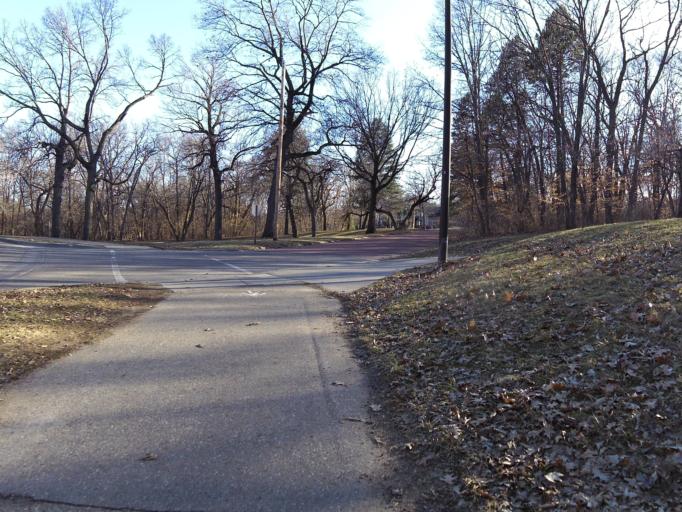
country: US
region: Minnesota
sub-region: Hennepin County
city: Saint Louis Park
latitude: 44.9318
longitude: -93.3095
